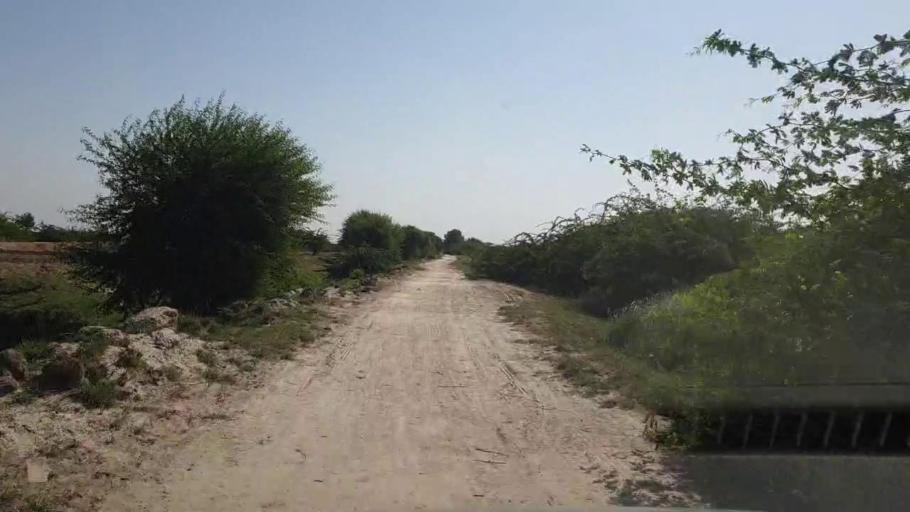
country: PK
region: Sindh
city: Kadhan
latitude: 24.6311
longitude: 68.9931
